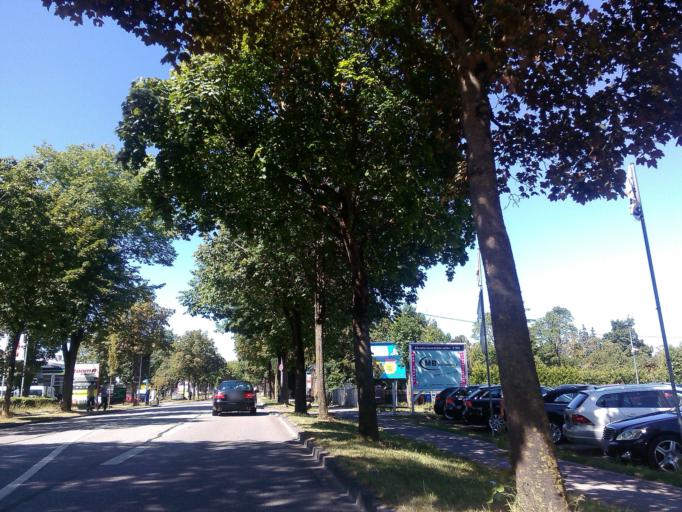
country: DE
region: Bavaria
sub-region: Upper Bavaria
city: Grafelfing
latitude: 48.1439
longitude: 11.4307
